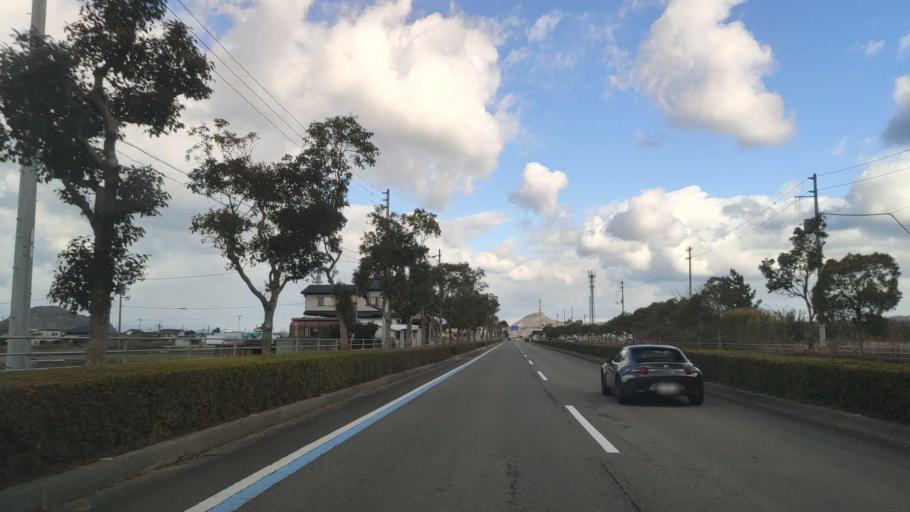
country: JP
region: Ehime
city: Hojo
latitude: 33.9504
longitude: 132.7743
